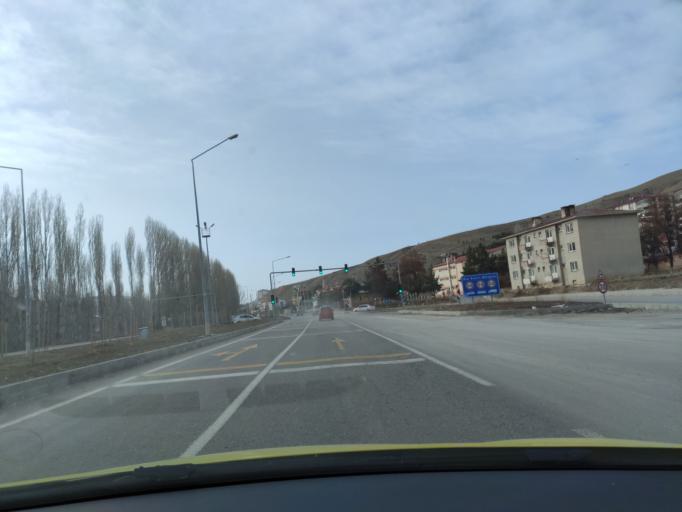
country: TR
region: Bayburt
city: Bayburt
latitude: 40.2407
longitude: 40.2473
